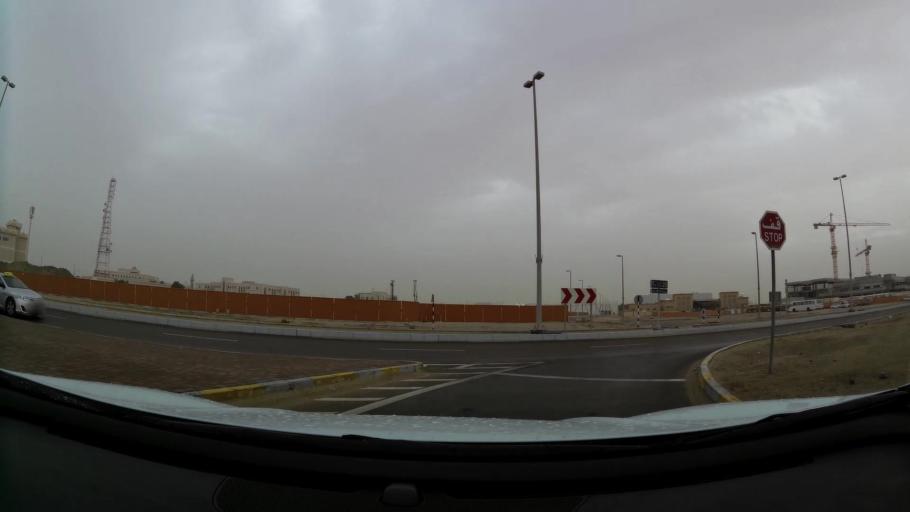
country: AE
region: Abu Dhabi
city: Abu Dhabi
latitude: 24.4309
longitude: 54.5802
